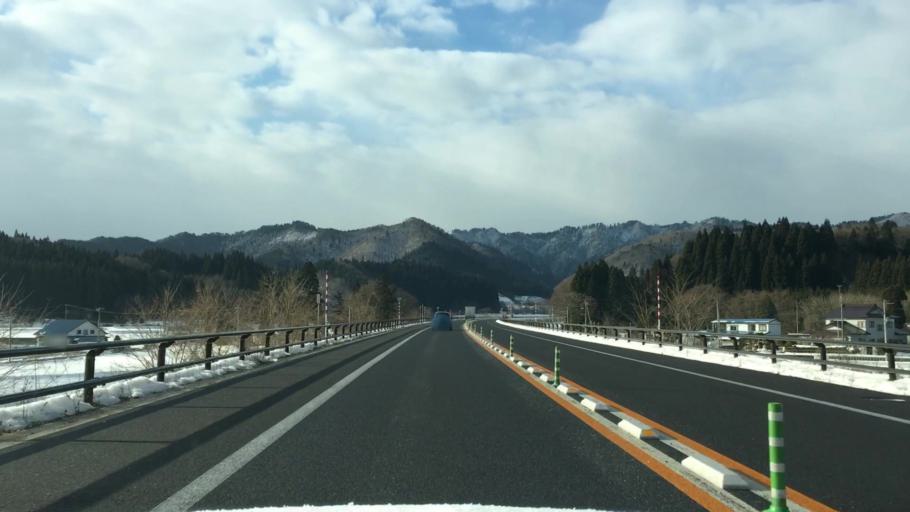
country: JP
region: Akita
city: Odate
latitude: 40.2389
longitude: 140.5040
